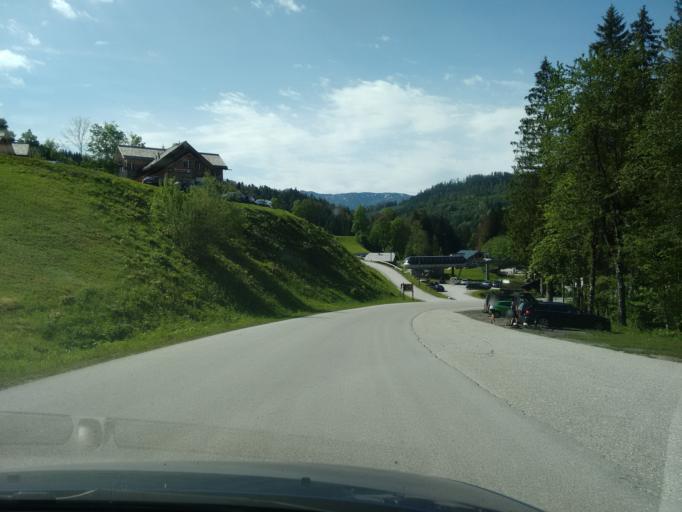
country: AT
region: Styria
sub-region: Politischer Bezirk Liezen
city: Altaussee
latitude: 47.6627
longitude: 13.7448
